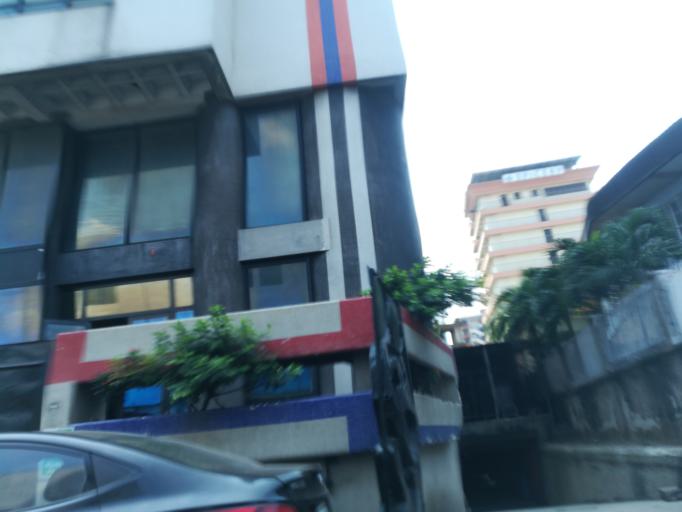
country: NG
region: Lagos
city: Lagos
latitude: 6.4501
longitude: 3.3948
